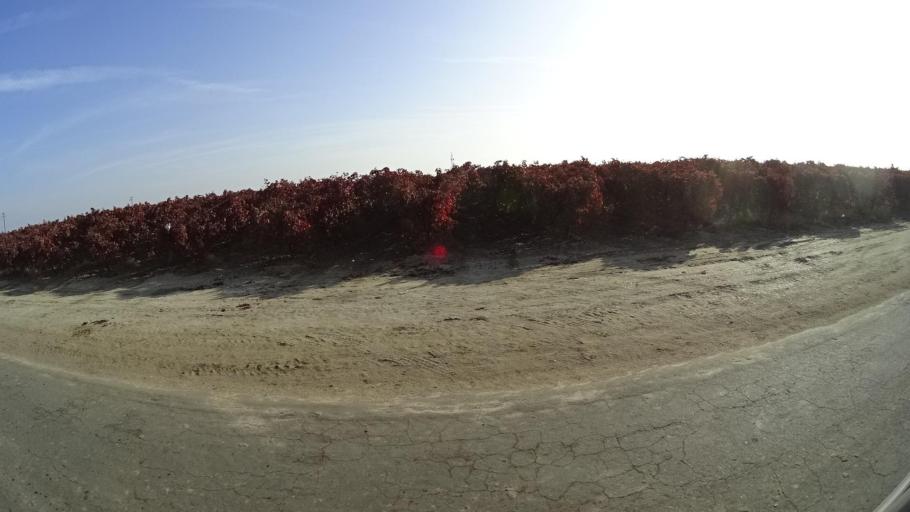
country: US
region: California
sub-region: Kern County
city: McFarland
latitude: 35.6876
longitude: -119.1870
